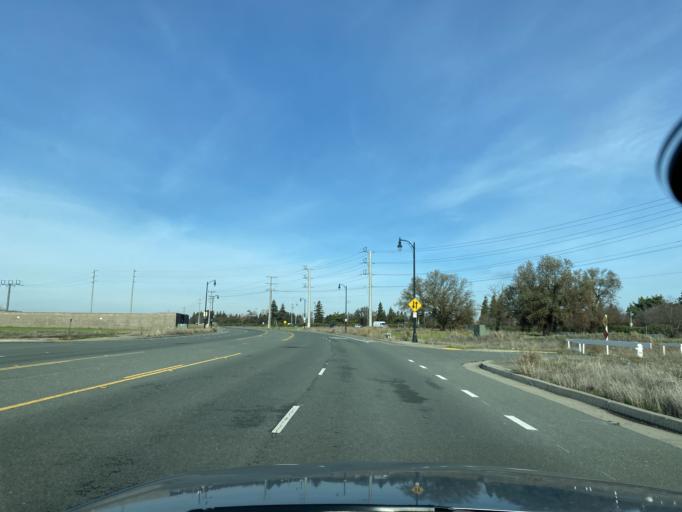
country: US
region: California
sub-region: Sacramento County
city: Elk Grove
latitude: 38.3858
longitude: -121.3728
